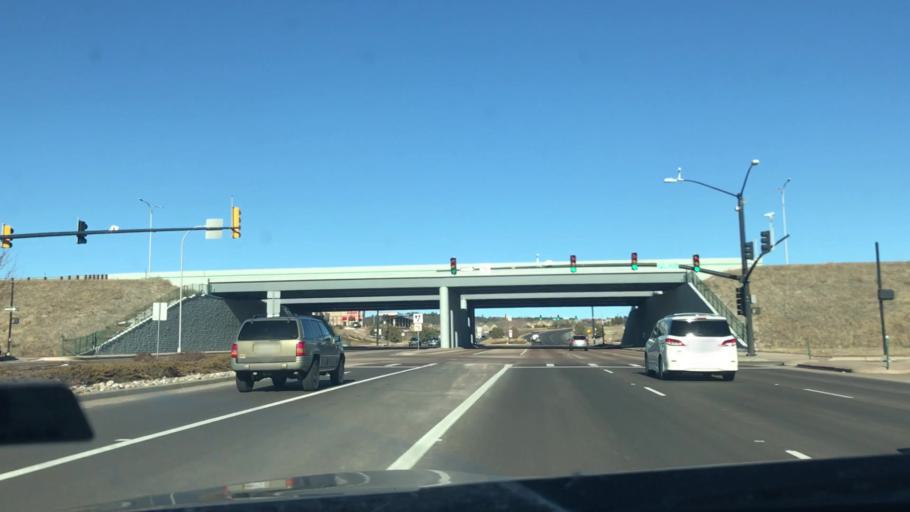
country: US
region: Colorado
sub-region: El Paso County
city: Black Forest
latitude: 38.9678
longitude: -104.7440
